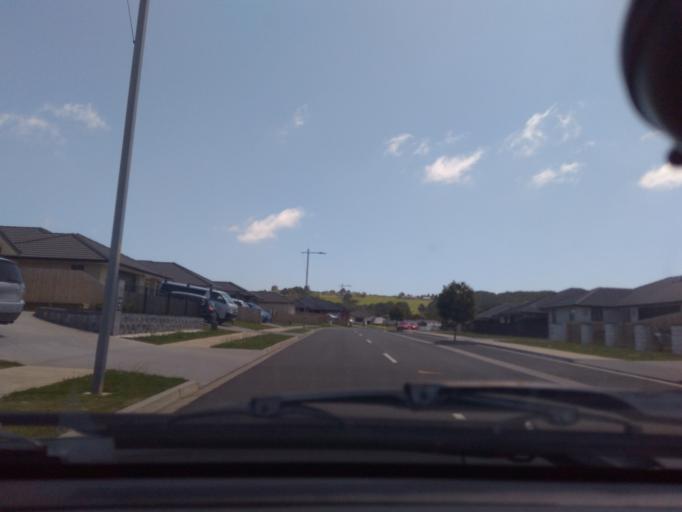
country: NZ
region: Northland
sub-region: Whangarei
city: Whangarei
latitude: -35.6752
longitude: 174.3194
